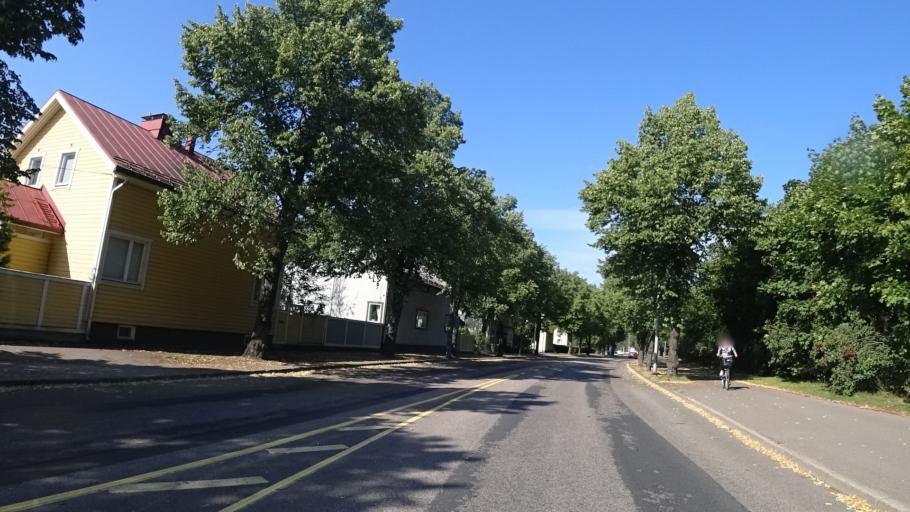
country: FI
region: Kymenlaakso
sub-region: Kotka-Hamina
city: Hamina
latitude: 60.5637
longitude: 27.2035
